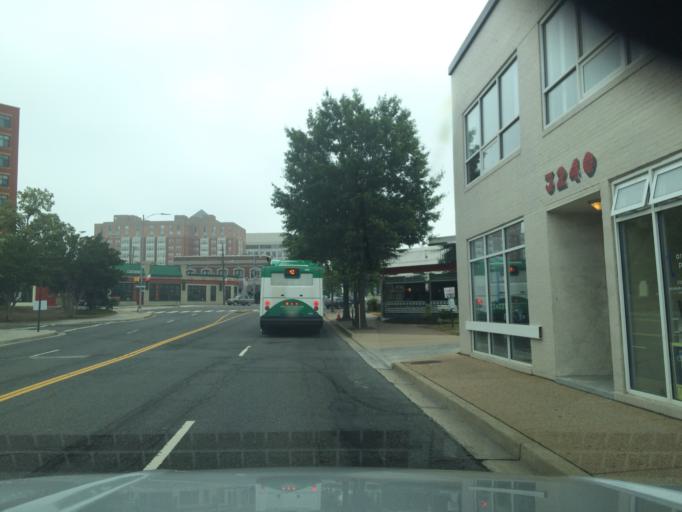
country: US
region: Virginia
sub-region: Arlington County
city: Arlington
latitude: 38.8853
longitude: -77.0976
